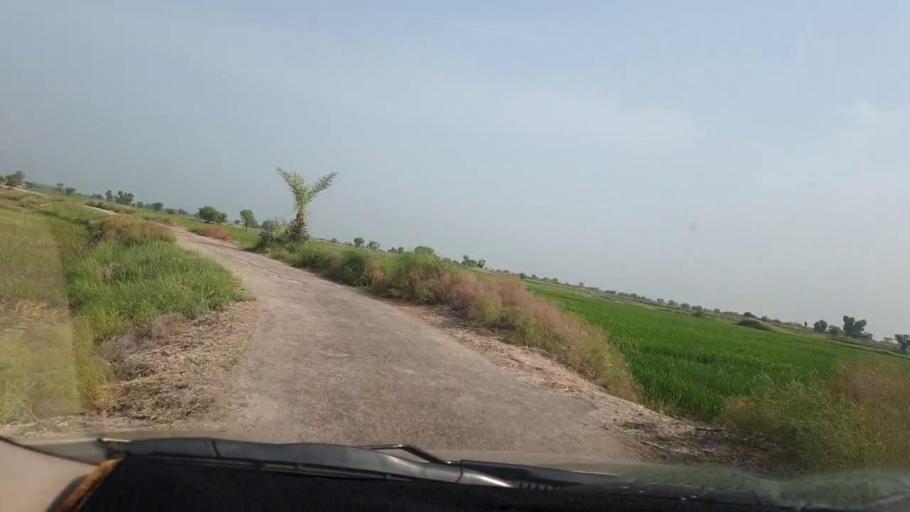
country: PK
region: Sindh
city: Goth Garelo
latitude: 27.4619
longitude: 68.0516
